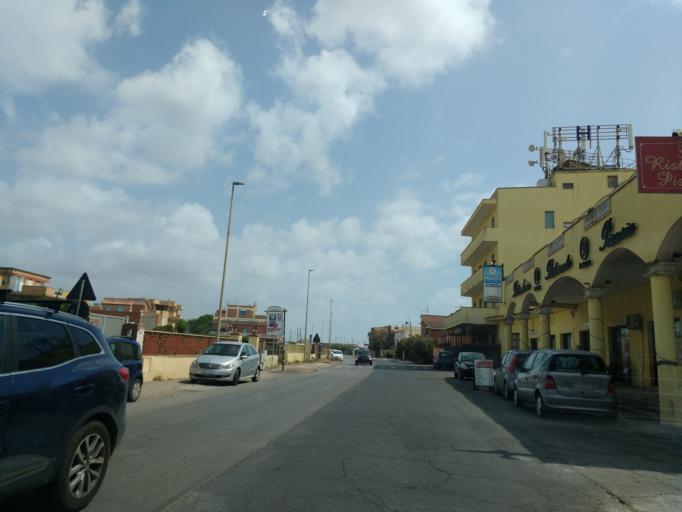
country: IT
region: Latium
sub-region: Citta metropolitana di Roma Capitale
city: Ardea
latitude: 41.5947
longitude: 12.4908
